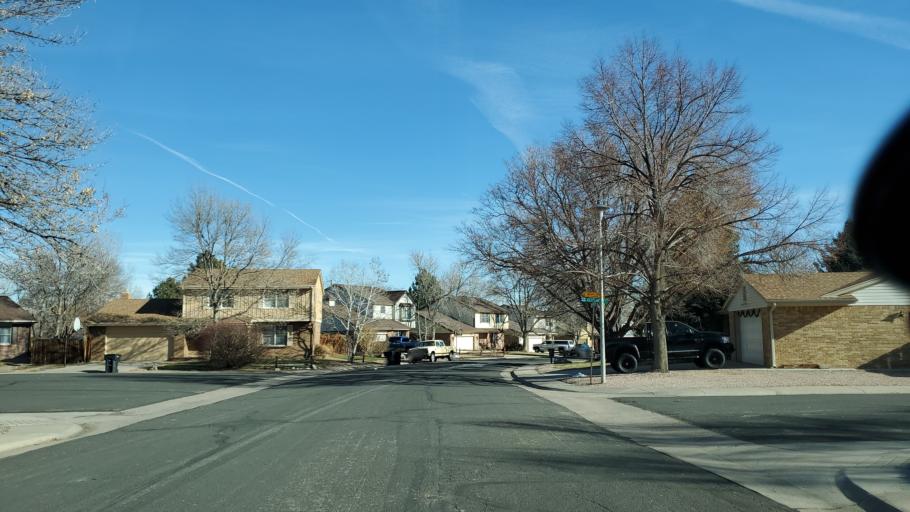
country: US
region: Colorado
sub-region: Adams County
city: Northglenn
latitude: 39.9204
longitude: -104.9542
